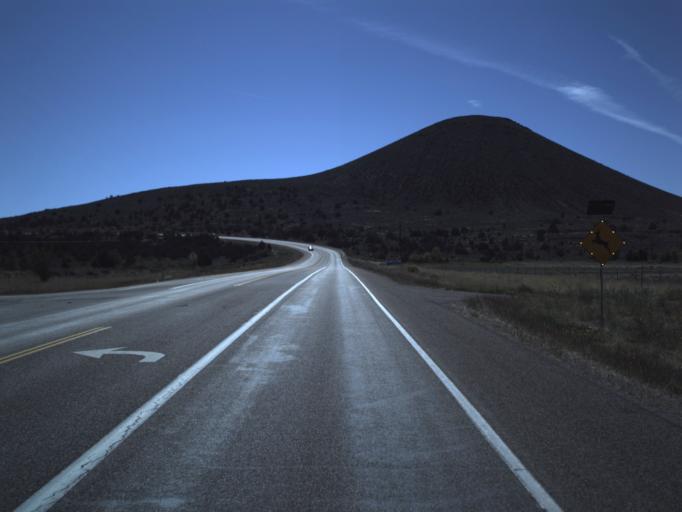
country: US
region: Utah
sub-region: Washington County
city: Ivins
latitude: 37.3296
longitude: -113.6933
